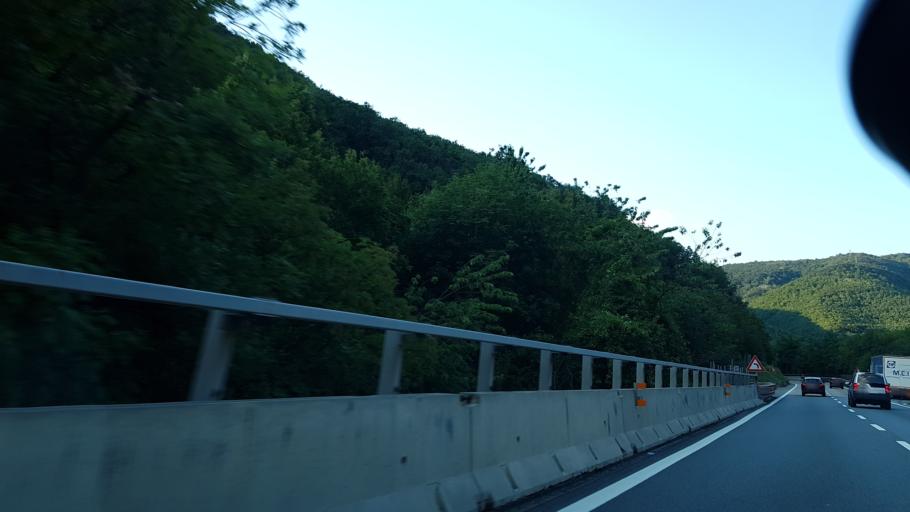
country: IT
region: Liguria
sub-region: Provincia di Genova
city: Isola del Cantone
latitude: 44.6591
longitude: 8.9262
